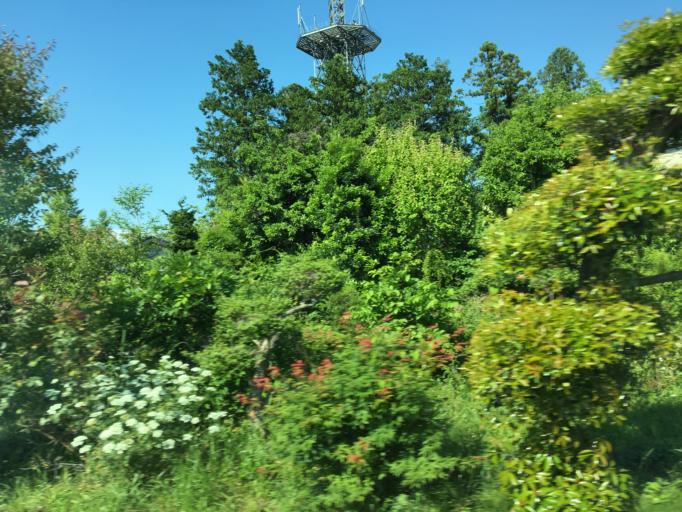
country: JP
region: Saitama
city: Morohongo
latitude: 35.9767
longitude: 139.3365
